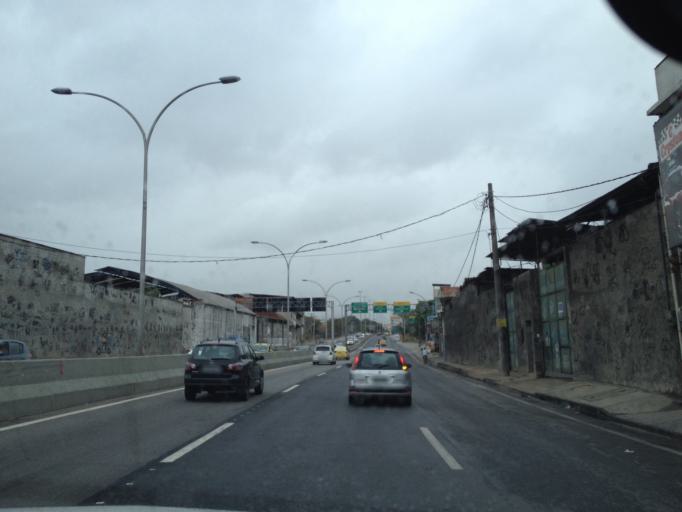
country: BR
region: Rio de Janeiro
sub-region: Rio De Janeiro
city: Rio de Janeiro
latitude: -22.8685
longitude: -43.2421
